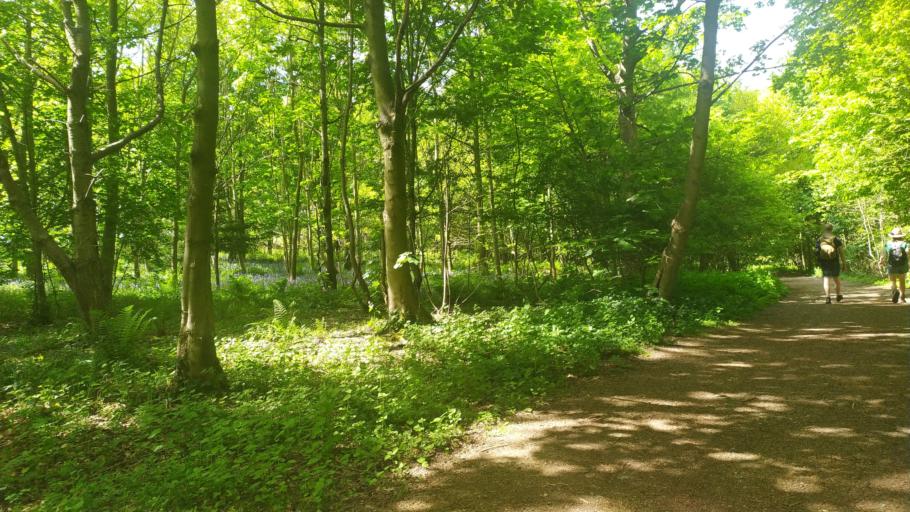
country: GB
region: England
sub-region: City and Borough of Leeds
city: Chapel Allerton
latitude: 53.8881
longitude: -1.5371
